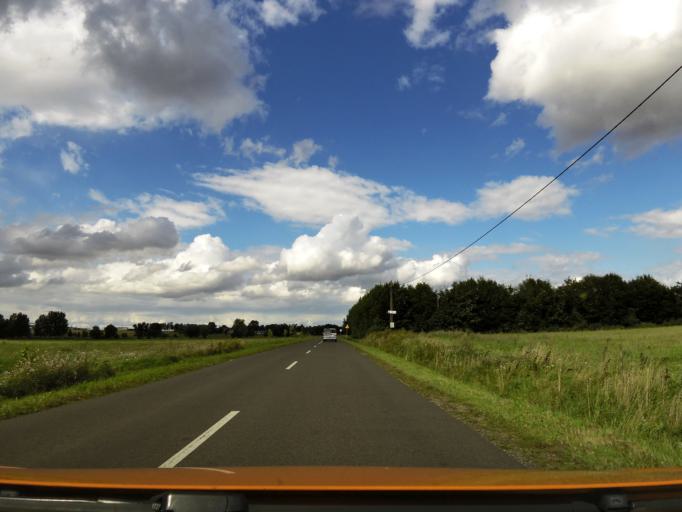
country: PL
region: West Pomeranian Voivodeship
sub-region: Powiat kolobrzeski
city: Ryman
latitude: 53.9839
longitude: 15.4909
